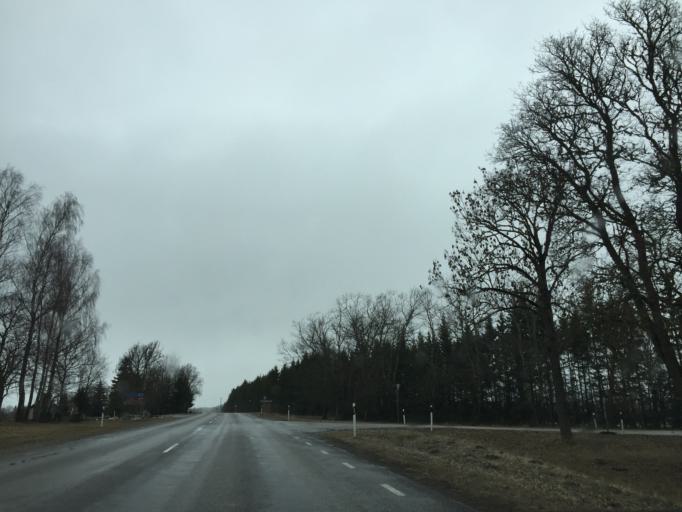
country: EE
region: Laeaene
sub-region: Ridala Parish
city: Uuemoisa
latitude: 58.8783
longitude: 23.6080
